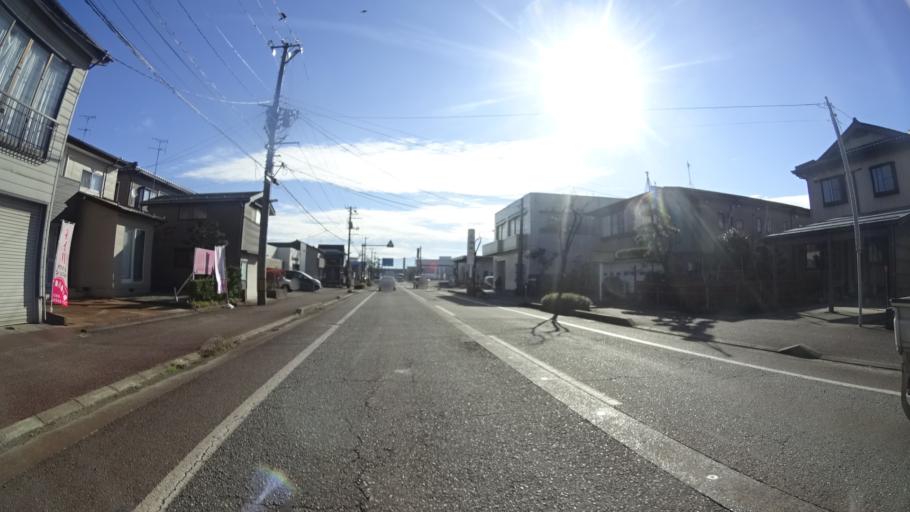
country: JP
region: Niigata
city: Mitsuke
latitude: 37.5432
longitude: 138.8872
